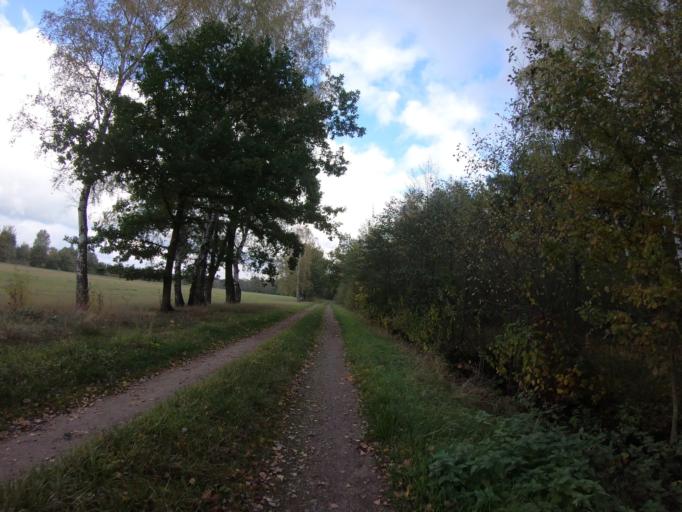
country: DE
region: Lower Saxony
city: Wahrenholz
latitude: 52.5808
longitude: 10.6152
